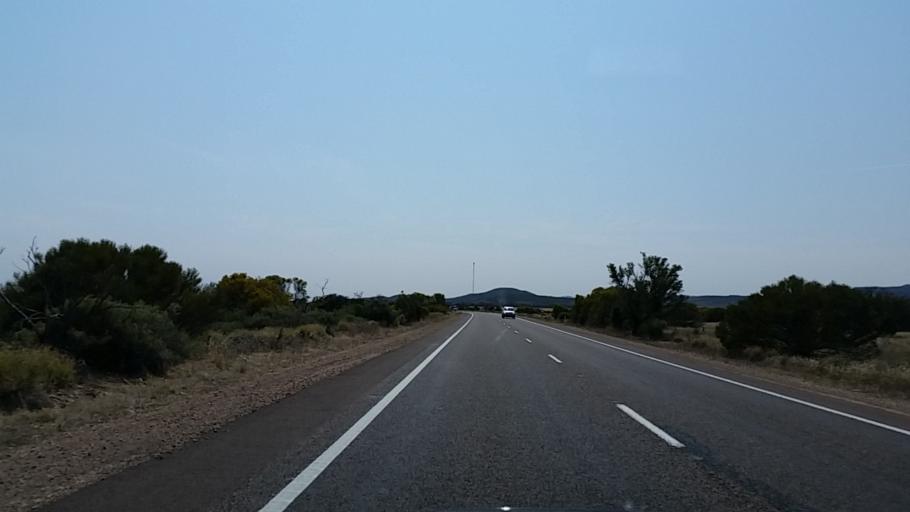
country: AU
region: South Australia
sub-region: Port Pirie City and Dists
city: Port Pirie
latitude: -32.8393
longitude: 137.9813
